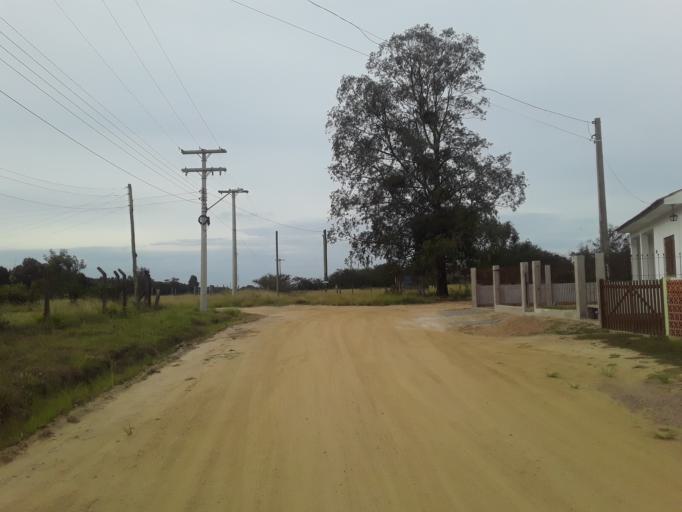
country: BR
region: Rio Grande do Sul
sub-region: Sao Lourenco Do Sul
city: Sao Lourenco do Sul
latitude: -31.3545
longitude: -51.9856
